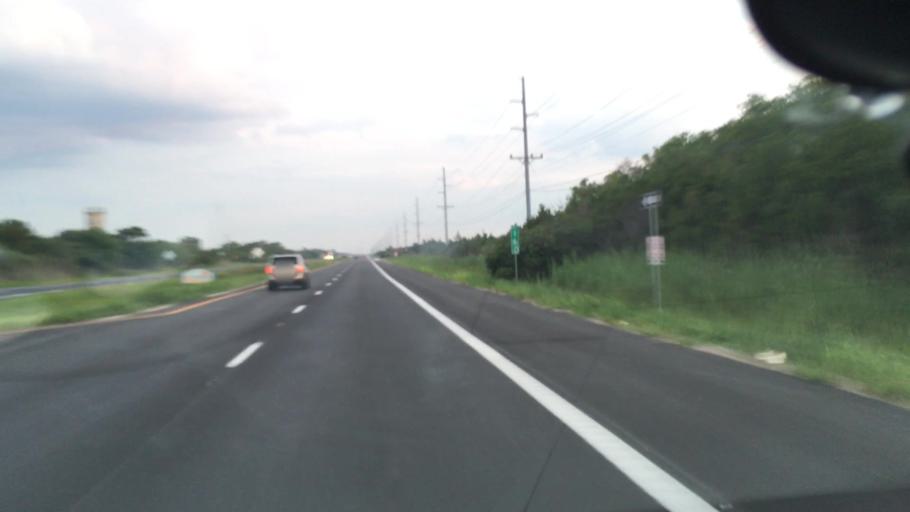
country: US
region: Delaware
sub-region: Sussex County
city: Rehoboth Beach
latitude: 38.6805
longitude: -75.0723
